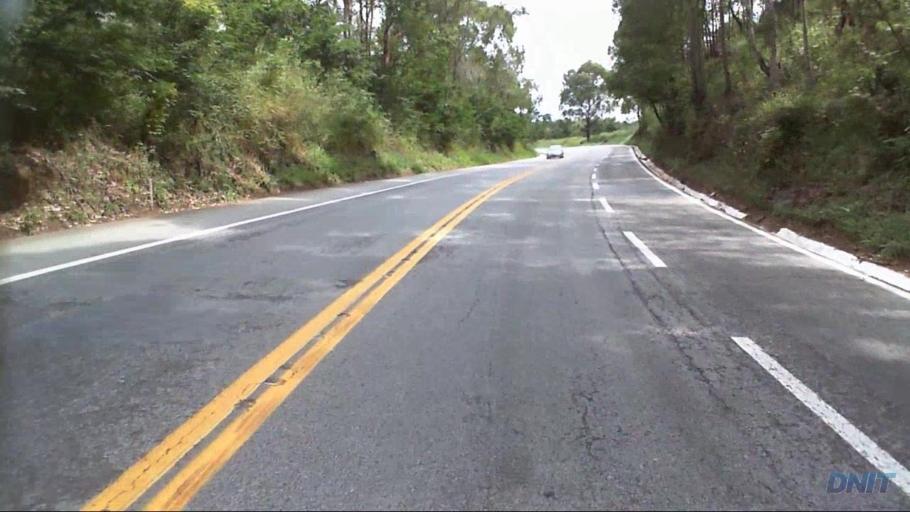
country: BR
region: Minas Gerais
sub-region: Caete
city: Caete
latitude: -19.7370
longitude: -43.6012
